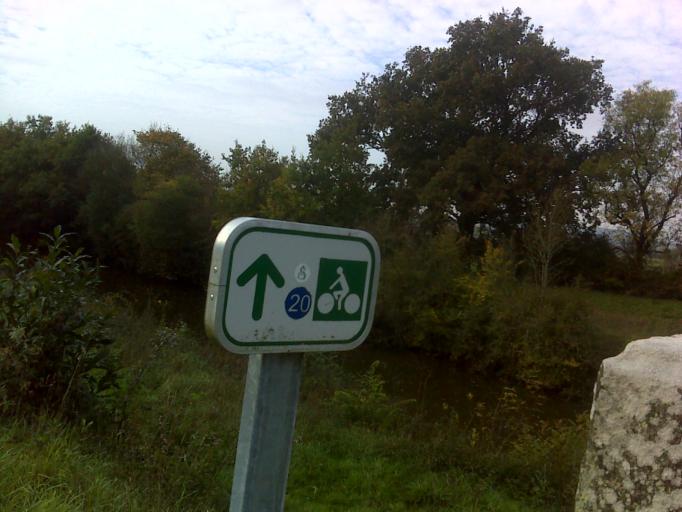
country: FR
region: Pays de la Loire
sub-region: Departement de la Loire-Atlantique
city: Saint-Nicolas-de-Redon
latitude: 47.6255
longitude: -2.0760
